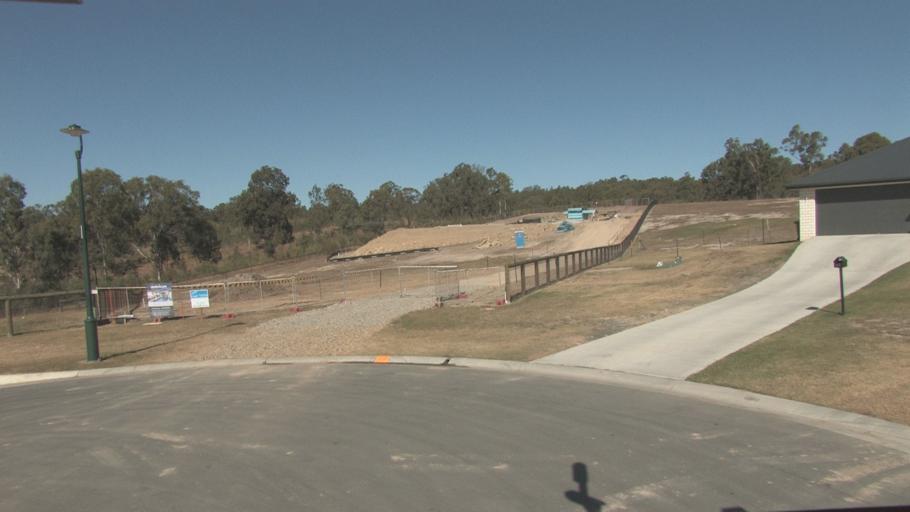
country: AU
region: Queensland
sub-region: Logan
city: Cedar Vale
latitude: -27.8746
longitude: 153.0420
